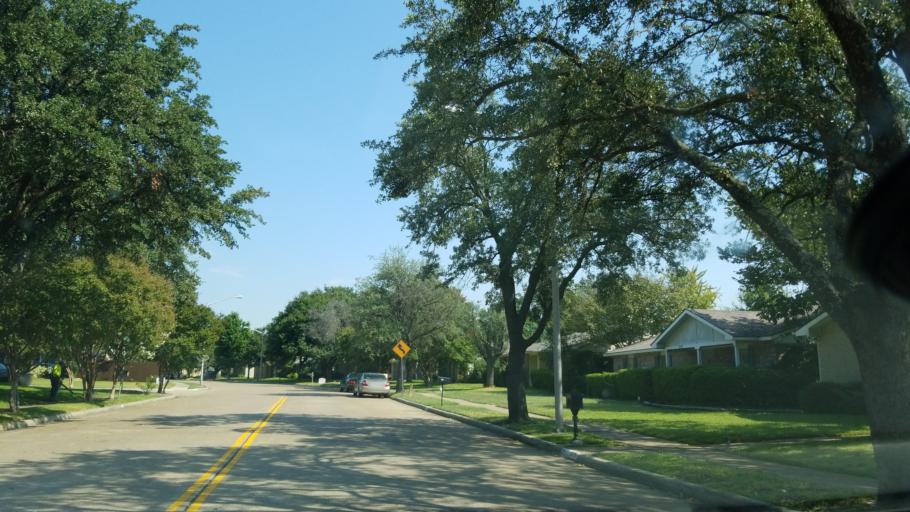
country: US
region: Texas
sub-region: Dallas County
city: Garland
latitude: 32.8745
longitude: -96.6939
